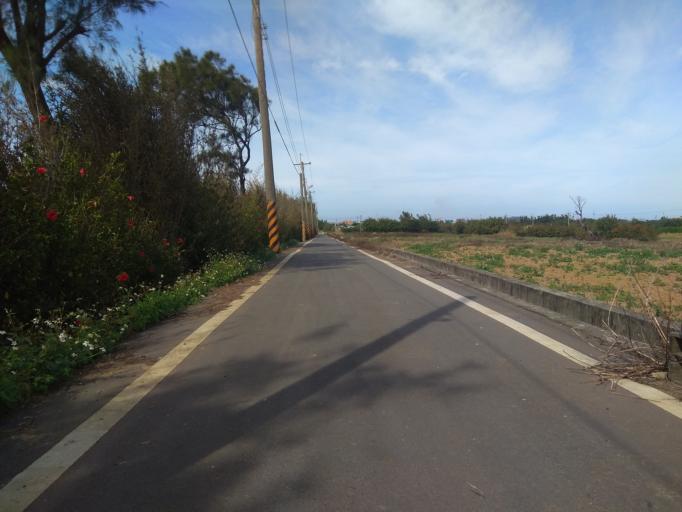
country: TW
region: Taiwan
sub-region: Hsinchu
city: Zhubei
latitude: 25.0124
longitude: 121.0785
